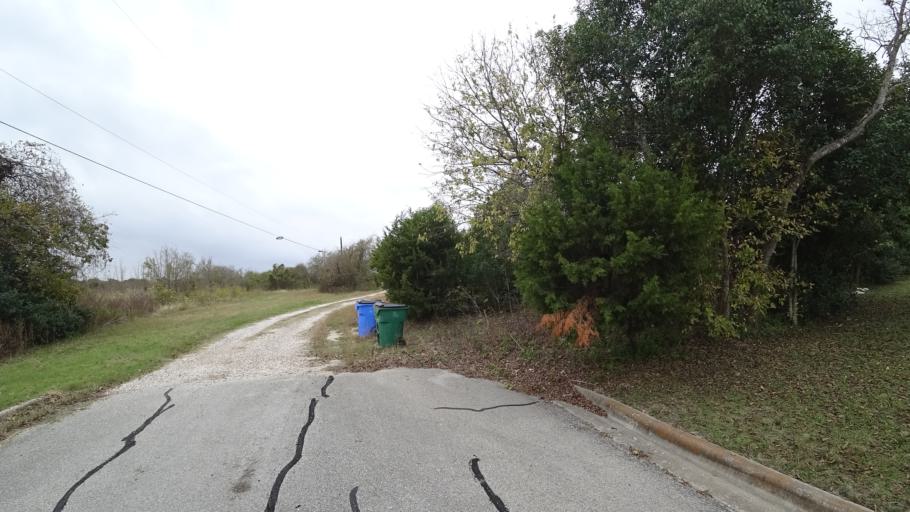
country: US
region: Texas
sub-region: Travis County
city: Pflugerville
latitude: 30.4360
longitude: -97.6177
